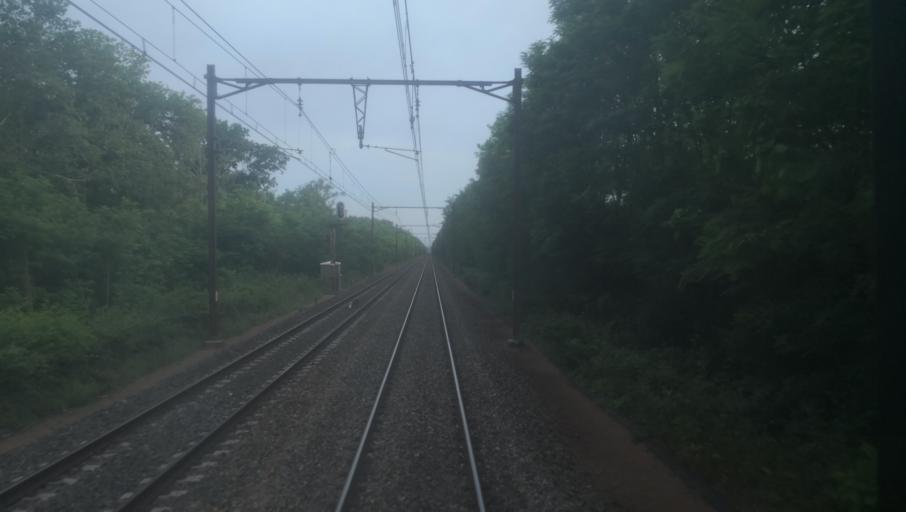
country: FR
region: Centre
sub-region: Departement du Loiret
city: Menestreau-en-Villette
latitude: 47.6523
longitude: 1.9806
